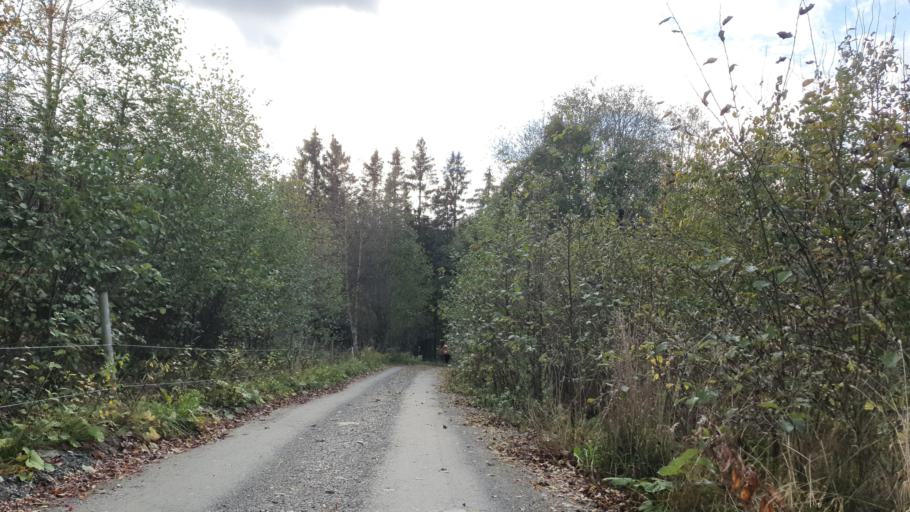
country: NO
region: Sor-Trondelag
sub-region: Klaebu
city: Klaebu
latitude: 63.2915
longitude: 10.4629
